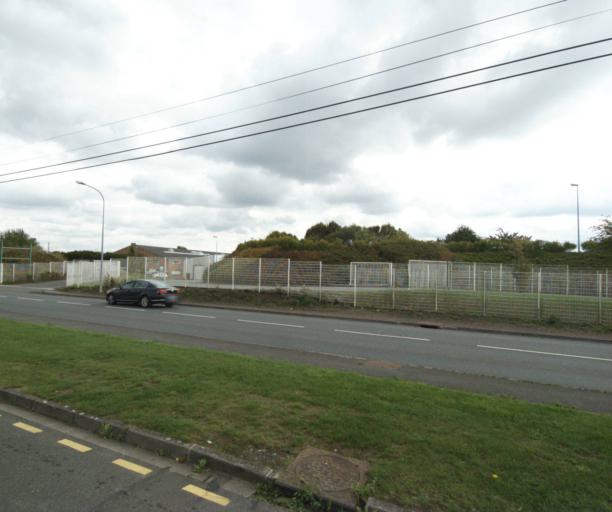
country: FR
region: Nord-Pas-de-Calais
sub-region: Departement du Nord
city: Lompret
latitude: 50.6652
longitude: 2.9819
